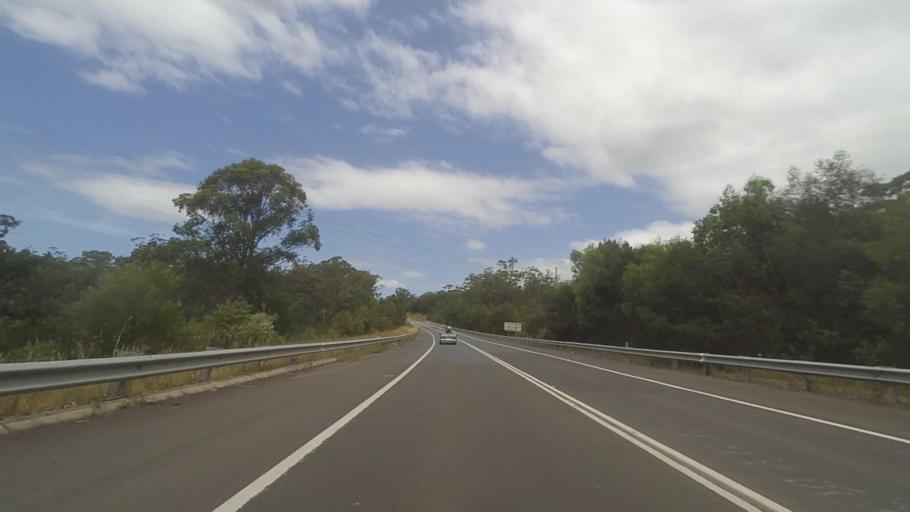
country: AU
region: New South Wales
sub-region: Shoalhaven Shire
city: Milton
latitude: -35.2144
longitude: 150.4351
